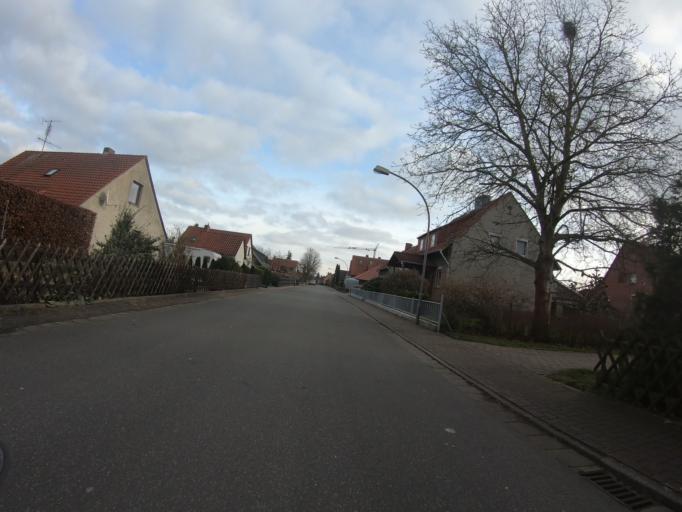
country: DE
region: Lower Saxony
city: Sassenburg
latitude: 52.5109
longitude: 10.5876
